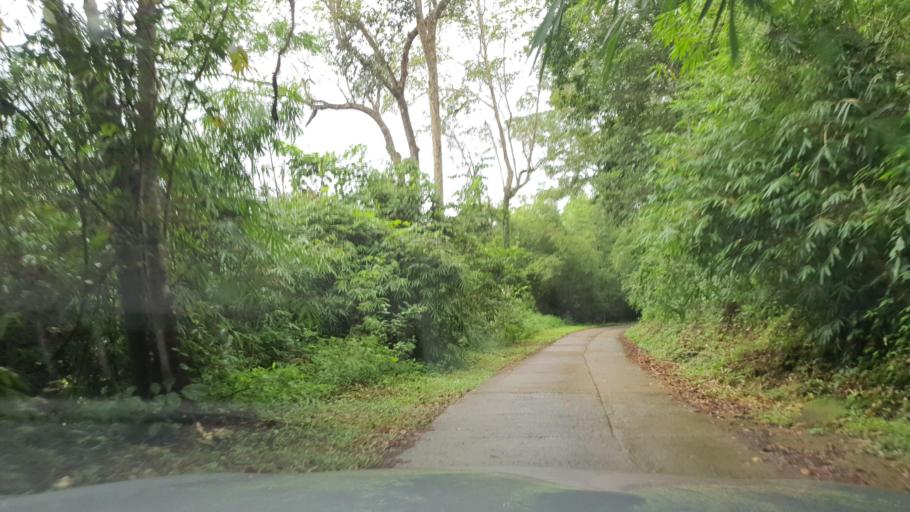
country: TH
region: Chiang Mai
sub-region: Amphoe Chiang Dao
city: Chiang Dao
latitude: 19.2769
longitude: 98.9594
